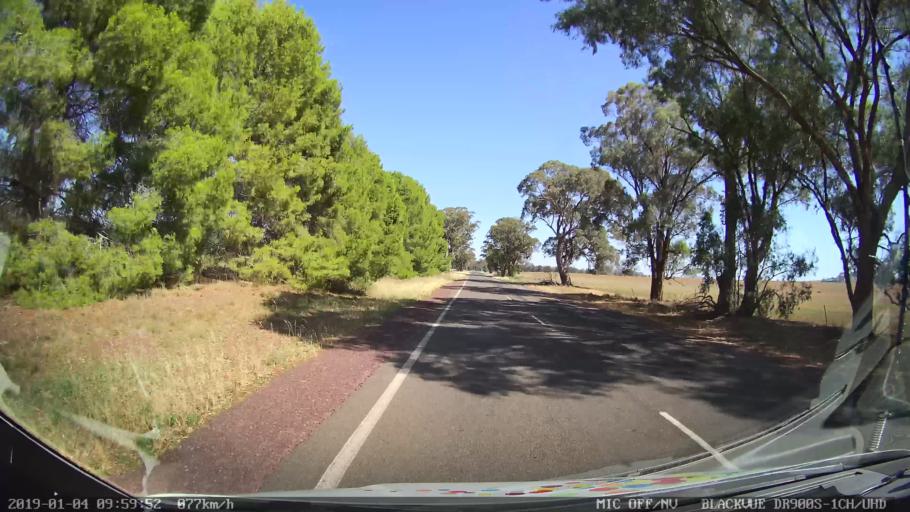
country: AU
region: New South Wales
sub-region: Cabonne
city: Canowindra
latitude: -33.5034
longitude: 148.3831
